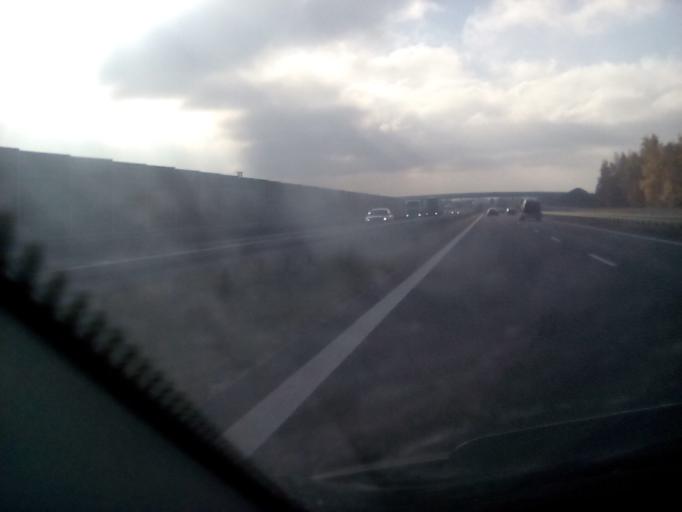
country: PL
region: Masovian Voivodeship
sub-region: Powiat bialobrzeski
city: Promna
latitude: 51.7128
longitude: 20.9244
